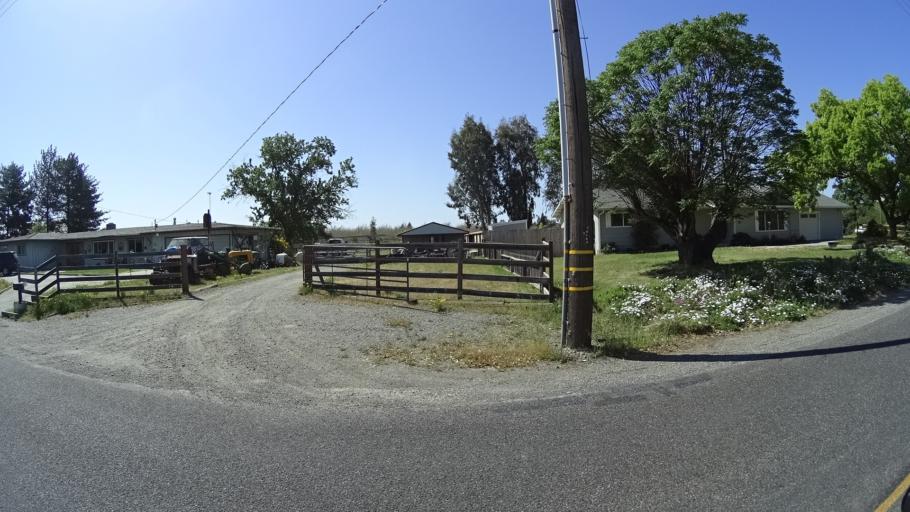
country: US
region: California
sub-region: Glenn County
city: Orland
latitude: 39.7256
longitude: -122.1824
